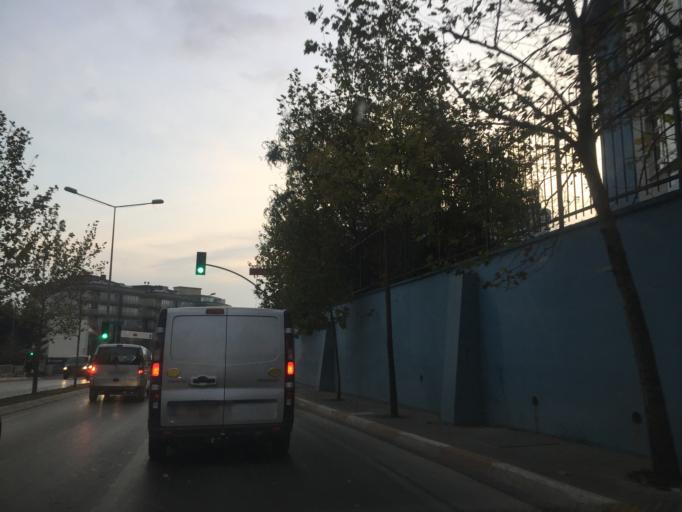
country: TR
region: Istanbul
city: Samandira
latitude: 40.9823
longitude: 29.2215
